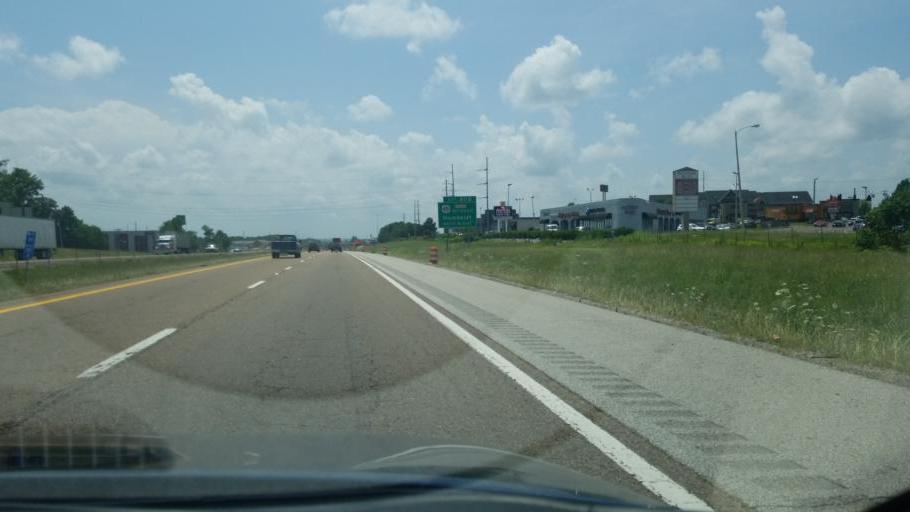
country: US
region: Tennessee
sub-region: Madison County
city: Jackson
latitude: 35.6661
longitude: -88.8466
